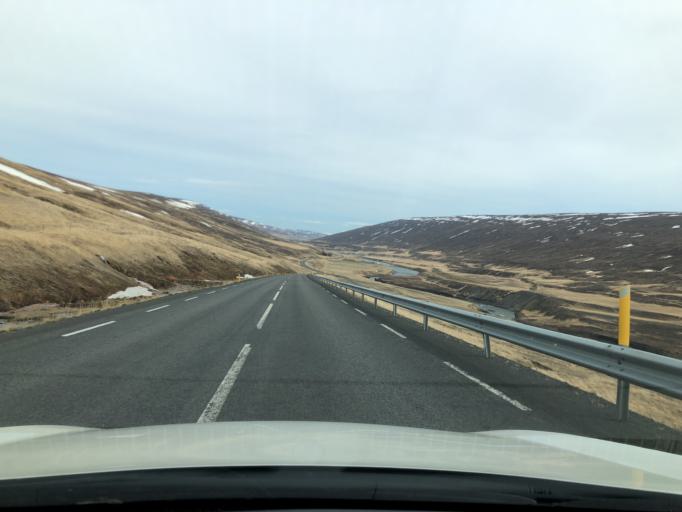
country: IS
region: East
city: Egilsstadir
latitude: 65.3075
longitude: -15.1659
